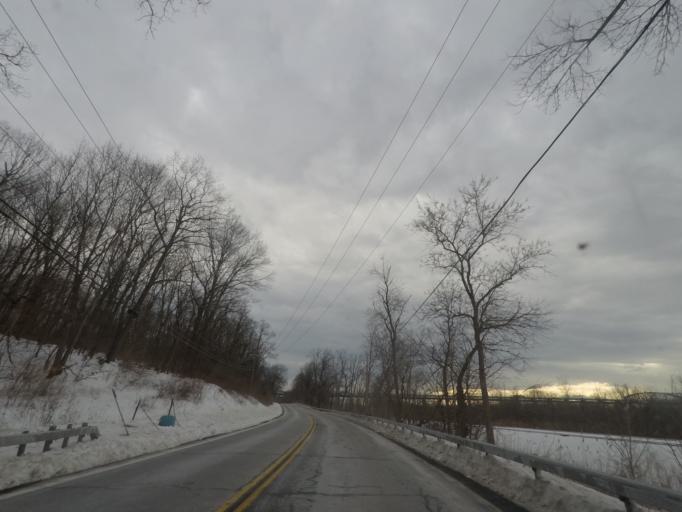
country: US
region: New York
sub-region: Rensselaer County
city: Castleton-on-Hudson
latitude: 42.5139
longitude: -73.7630
